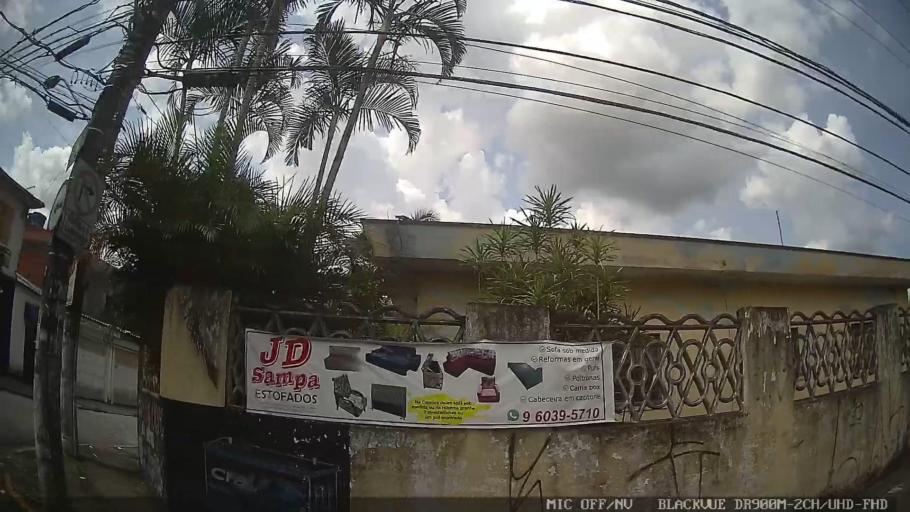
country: BR
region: Sao Paulo
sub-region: Poa
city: Poa
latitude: -23.5254
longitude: -46.3383
